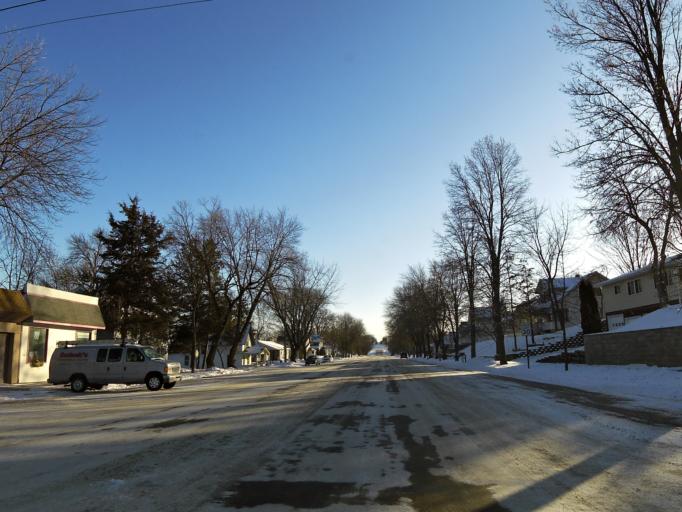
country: US
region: Minnesota
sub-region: Rice County
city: Lonsdale
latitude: 44.4796
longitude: -93.4286
